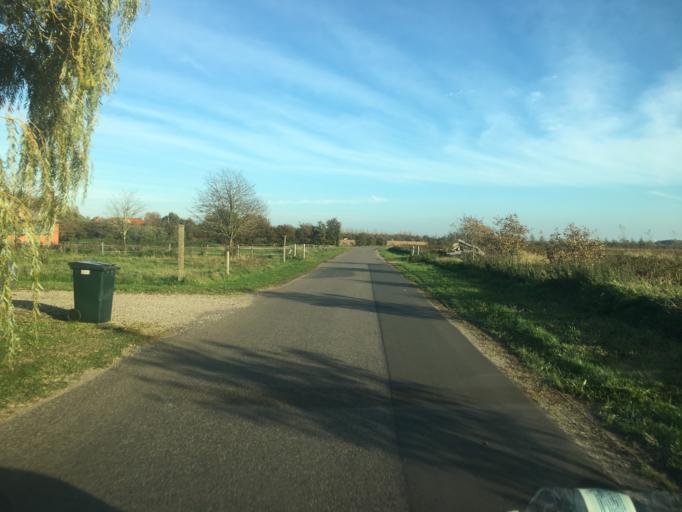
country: DE
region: Schleswig-Holstein
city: Ladelund
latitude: 54.9024
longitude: 9.0067
